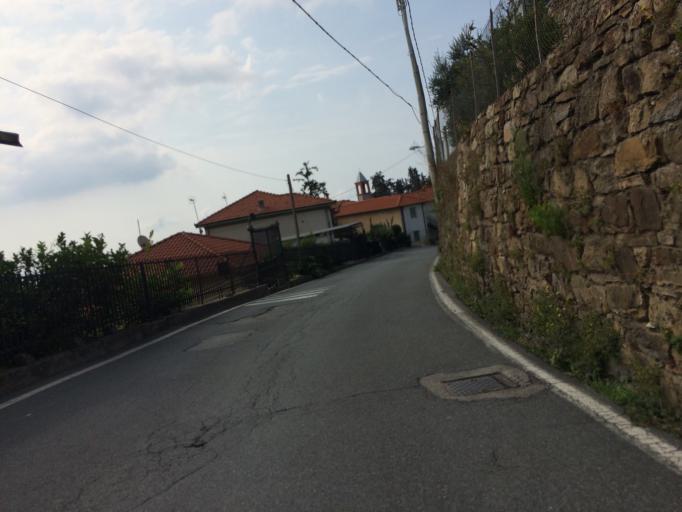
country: IT
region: Liguria
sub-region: Provincia di Imperia
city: San Remo
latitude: 43.8289
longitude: 7.7672
